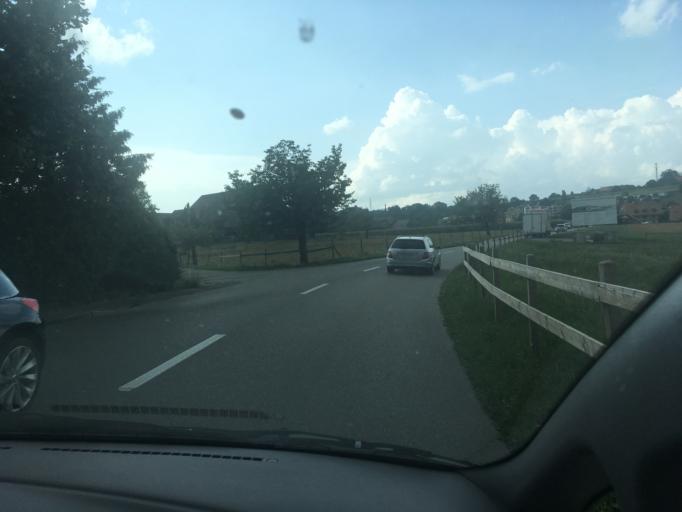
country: CH
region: Bern
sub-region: Bern-Mittelland District
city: Kirchlindach
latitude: 46.9909
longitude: 7.3994
